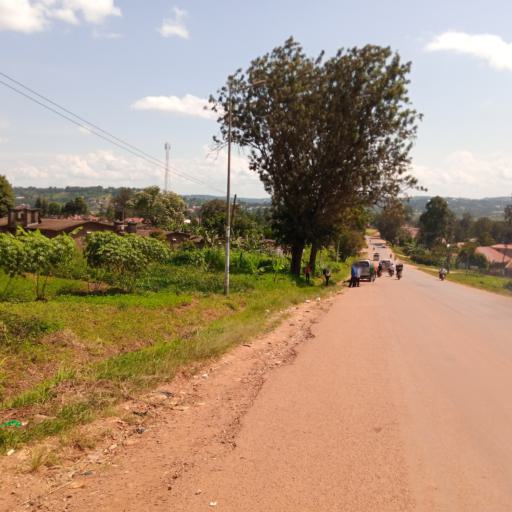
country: UG
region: Central Region
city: Masaka
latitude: -0.3432
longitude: 31.7332
